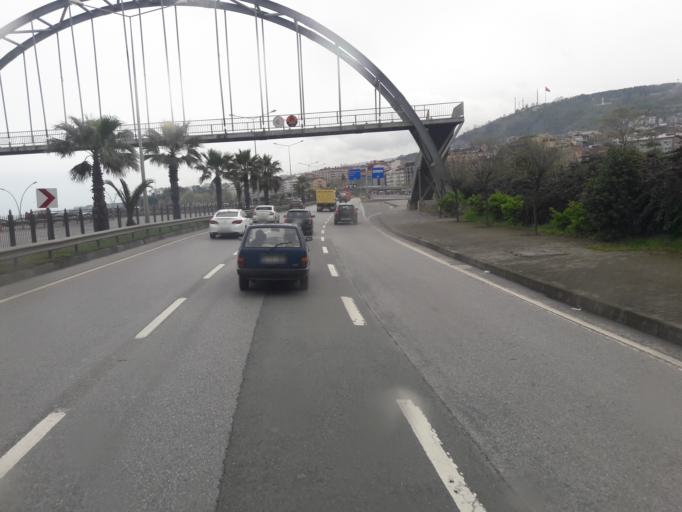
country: TR
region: Trabzon
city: Trabzon
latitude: 41.0116
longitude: 39.7229
